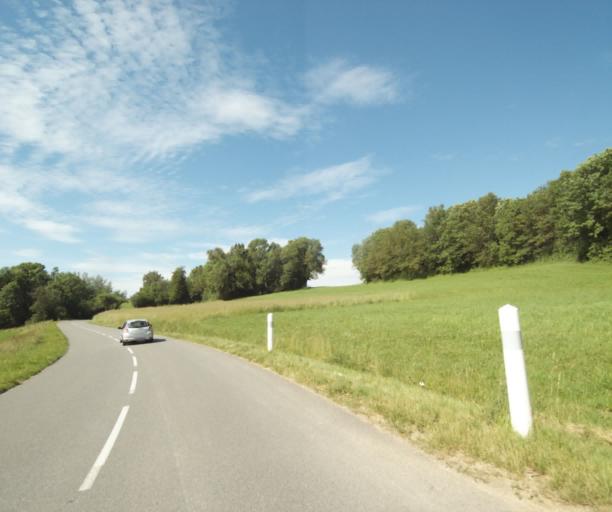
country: FR
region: Rhone-Alpes
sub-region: Departement de la Haute-Savoie
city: Allinges
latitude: 46.3132
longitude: 6.4796
